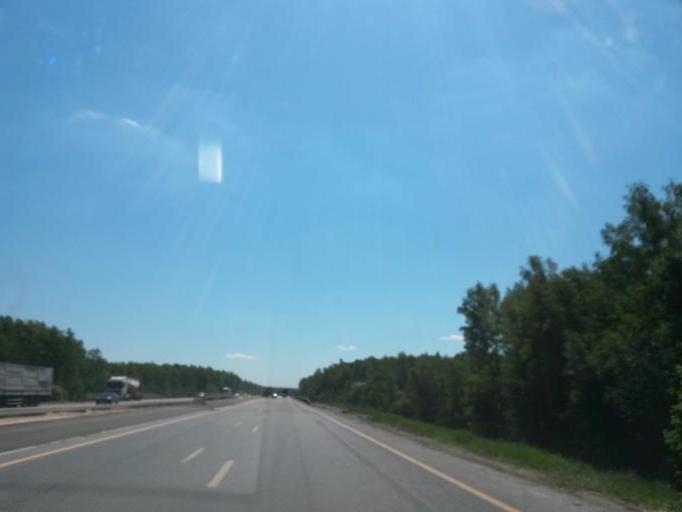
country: RU
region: Moskovskaya
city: Novyy Byt
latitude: 55.1210
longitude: 37.5730
